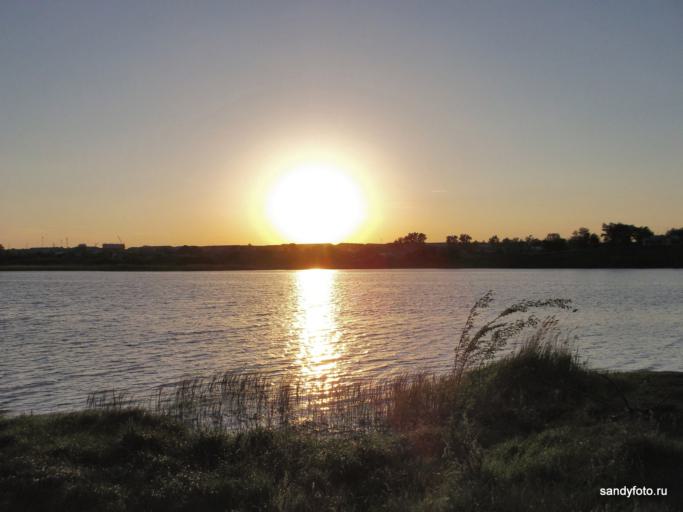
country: RU
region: Chelyabinsk
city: Troitsk
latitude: 54.0738
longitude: 61.5568
